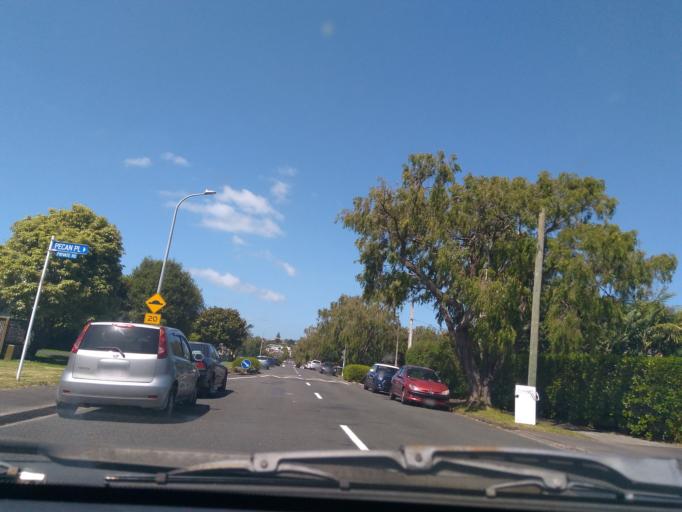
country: NZ
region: Auckland
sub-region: Auckland
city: Rosebank
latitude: -36.9005
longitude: 174.6907
